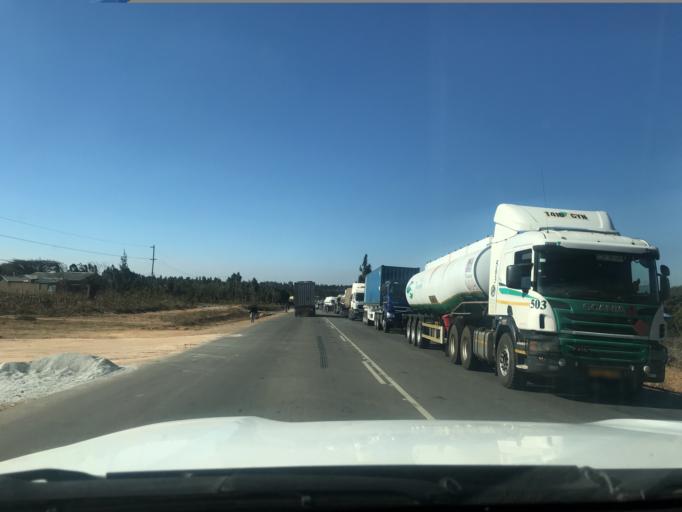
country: TZ
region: Njombe
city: Makumbako
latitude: -8.8133
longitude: 34.8418
